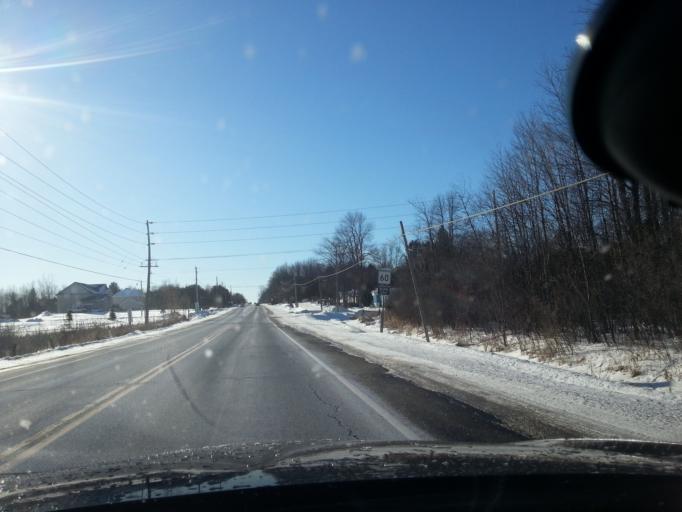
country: CA
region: Ontario
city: Ottawa
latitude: 45.2895
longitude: -75.5474
